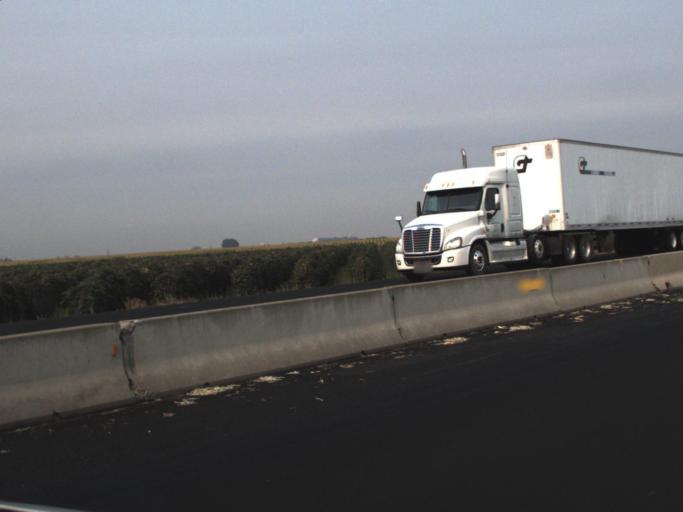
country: US
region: Washington
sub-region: Yakima County
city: Toppenish
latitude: 46.3877
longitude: -120.3544
